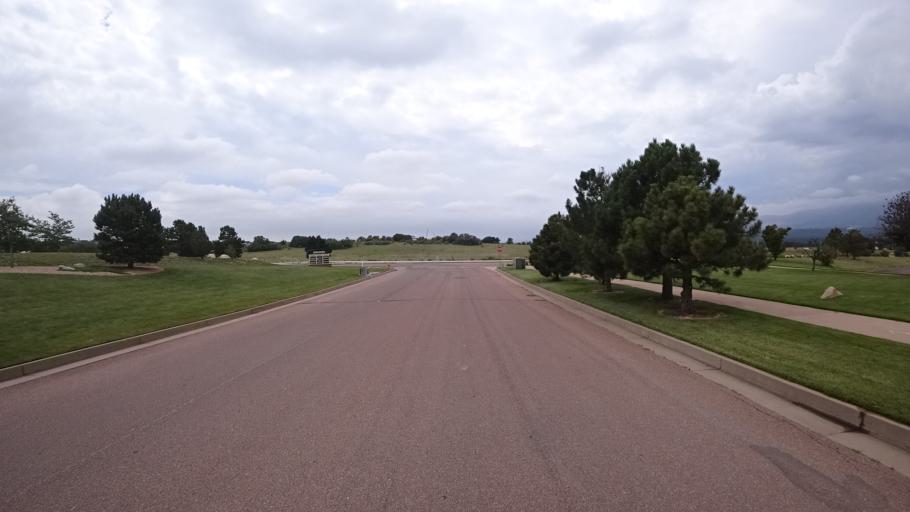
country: US
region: Colorado
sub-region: El Paso County
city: Gleneagle
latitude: 39.0106
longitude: -104.8163
